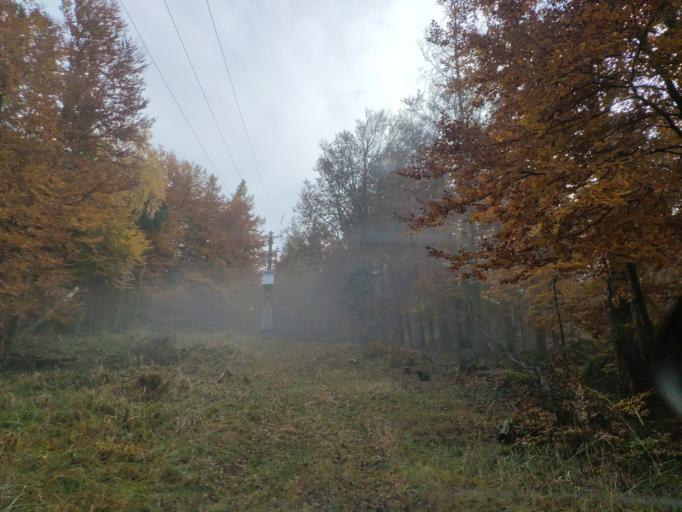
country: SK
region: Kosicky
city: Medzev
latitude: 48.7382
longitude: 20.9971
